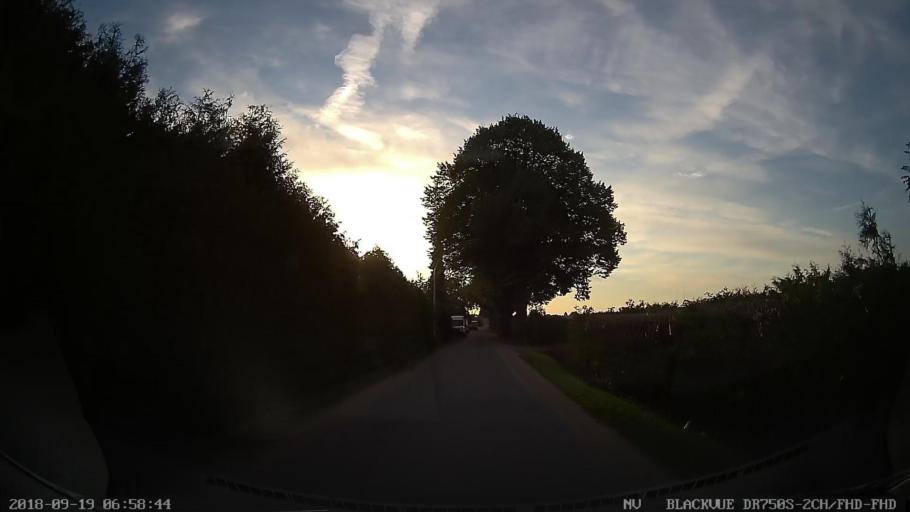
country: DE
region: Schleswig-Holstein
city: Ellerbek
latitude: 53.6331
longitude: 9.8841
